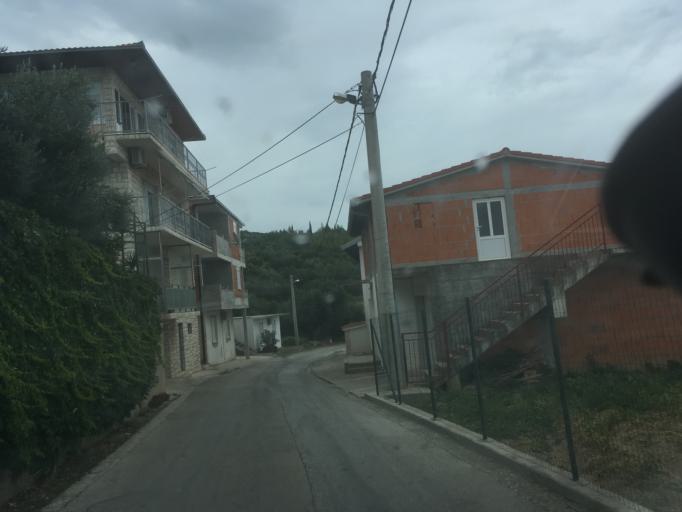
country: HR
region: Splitsko-Dalmatinska
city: Jesenice
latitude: 43.4554
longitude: 16.6230
